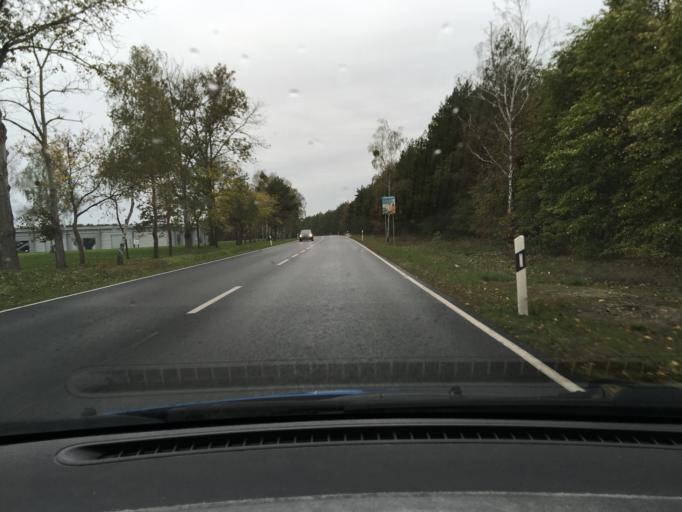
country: DE
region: Saxony-Anhalt
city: Klieken
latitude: 51.8936
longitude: 12.3676
